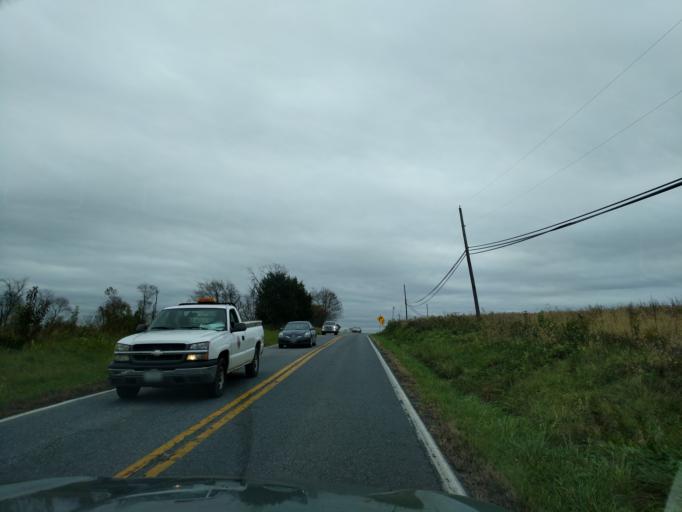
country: US
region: Maryland
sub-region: Frederick County
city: Spring Ridge
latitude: 39.4080
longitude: -77.2923
